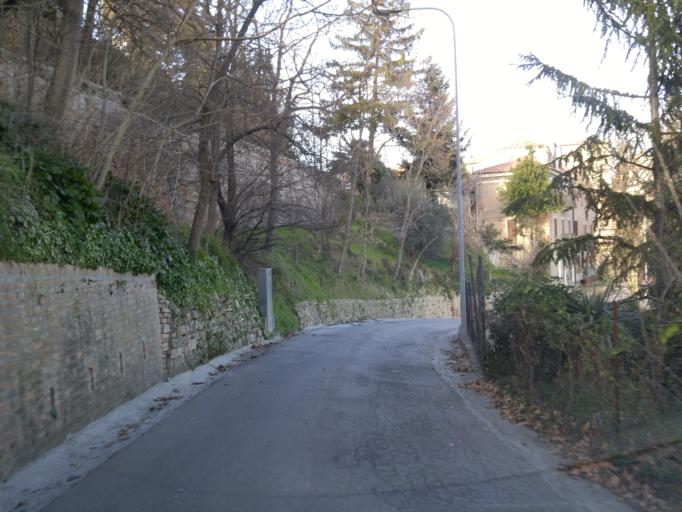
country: IT
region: The Marches
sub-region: Provincia di Pesaro e Urbino
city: Cartoceto
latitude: 43.7670
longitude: 12.8817
